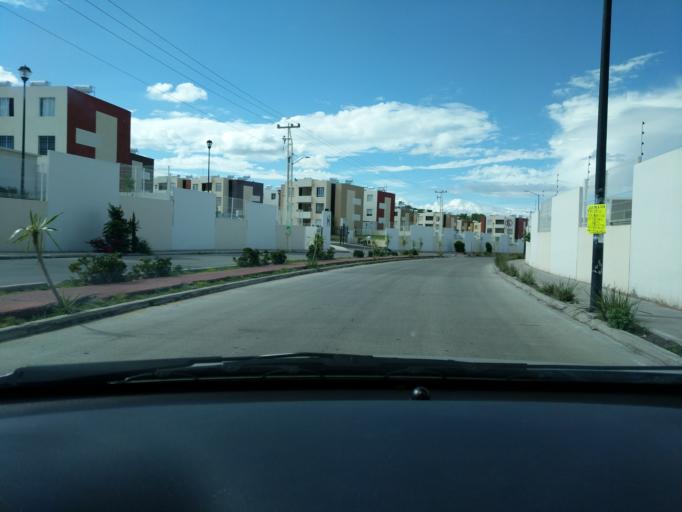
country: MX
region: Queretaro
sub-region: El Marques
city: La Loma
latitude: 20.5864
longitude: -100.2625
